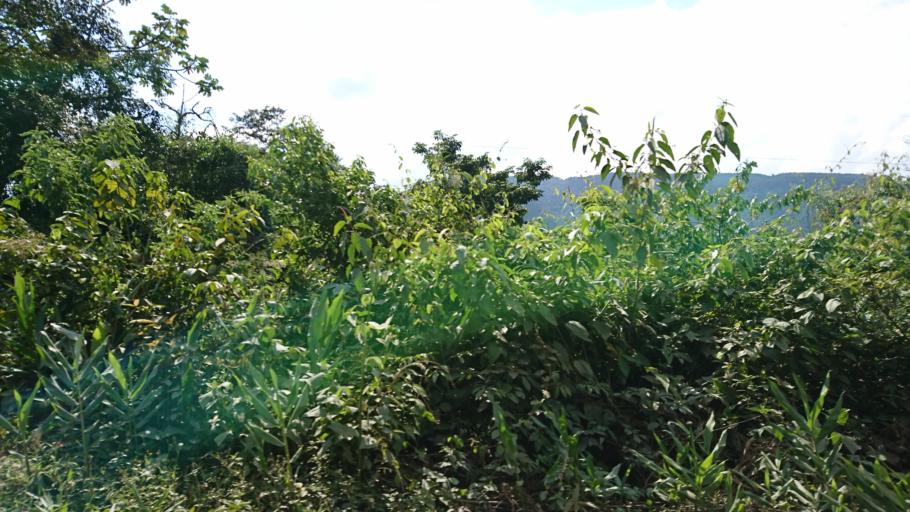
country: BO
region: La Paz
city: Coroico
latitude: -16.1374
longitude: -67.7495
